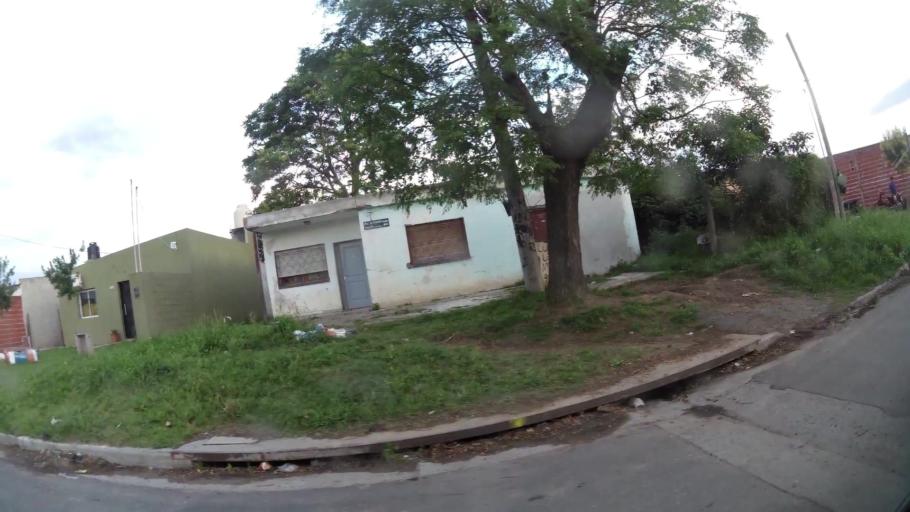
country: AR
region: Buenos Aires
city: San Nicolas de los Arroyos
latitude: -33.3162
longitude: -60.2384
